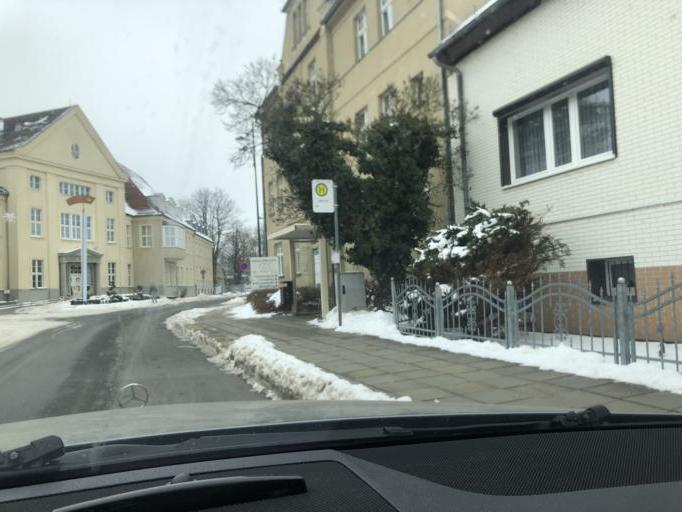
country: DE
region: Brandenburg
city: Guben
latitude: 51.9466
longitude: 14.7144
